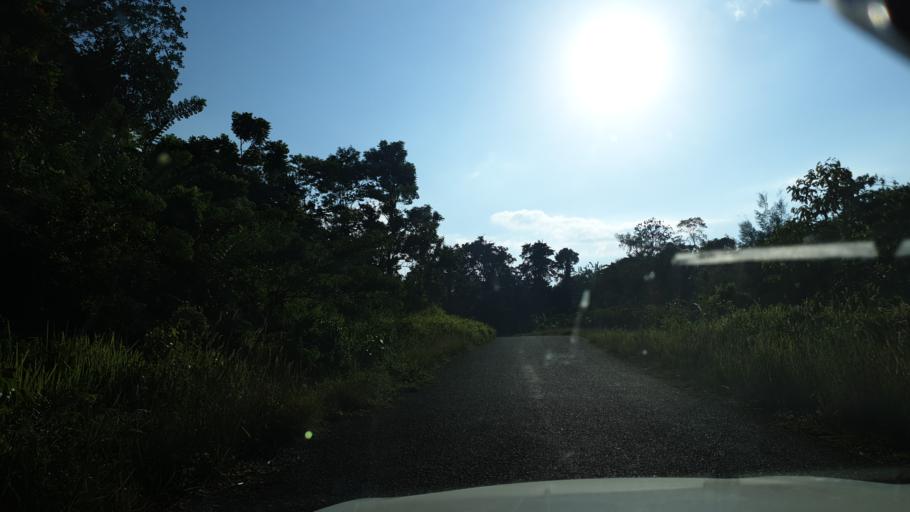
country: PG
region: East Sepik
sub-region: Wewak
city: Wewak
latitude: -3.6926
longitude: 143.6537
